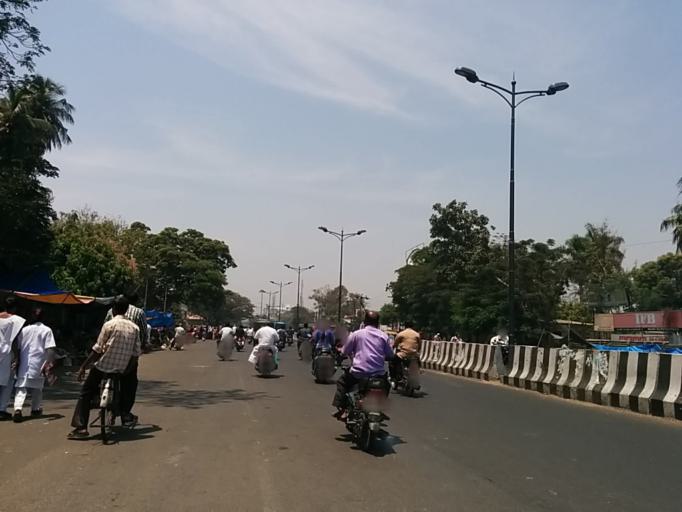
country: IN
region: Pondicherry
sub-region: Puducherry
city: Puducherry
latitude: 11.9304
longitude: 79.8229
